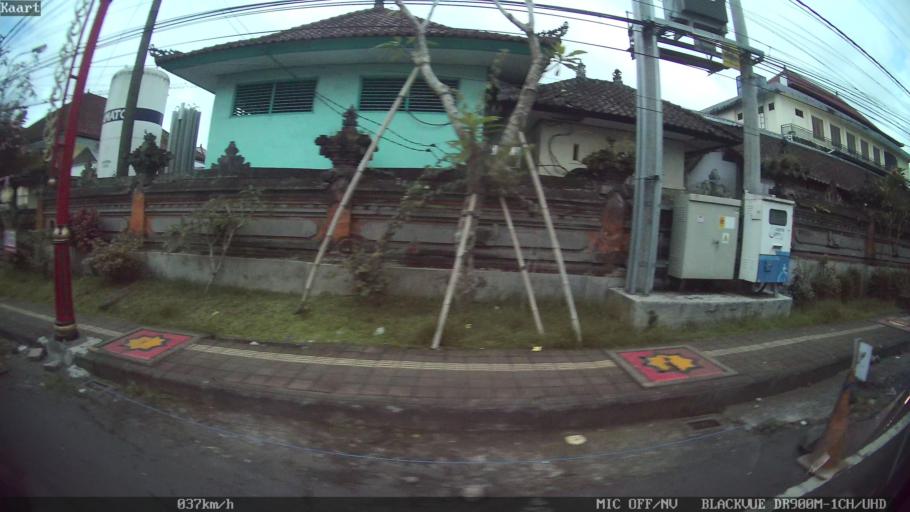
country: ID
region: Bali
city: Bangli
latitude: -8.4564
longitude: 115.3529
